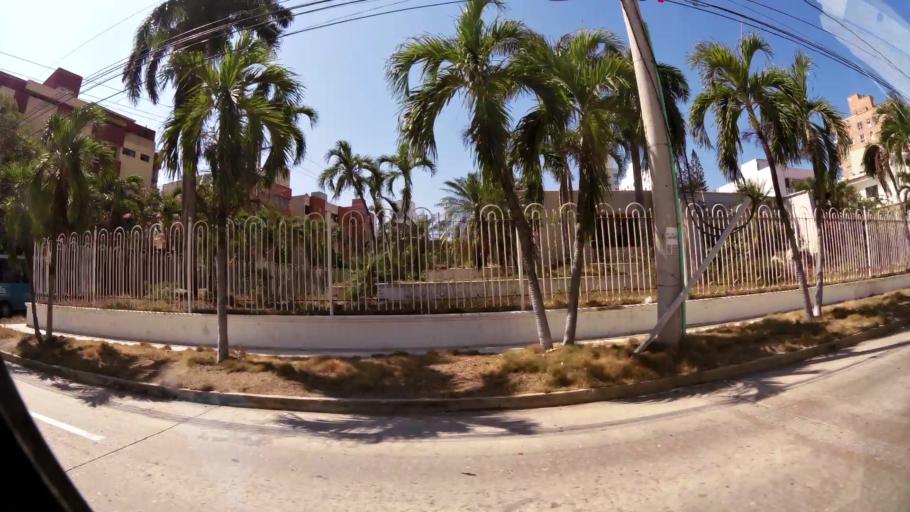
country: CO
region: Atlantico
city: Barranquilla
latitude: 11.0169
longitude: -74.8198
